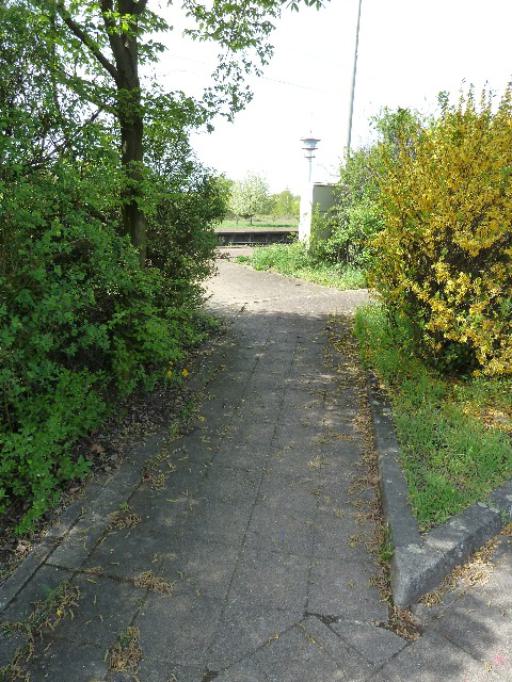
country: DE
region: Baden-Wuerttemberg
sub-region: Karlsruhe Region
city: Waghausel
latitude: 49.2262
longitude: 8.5027
